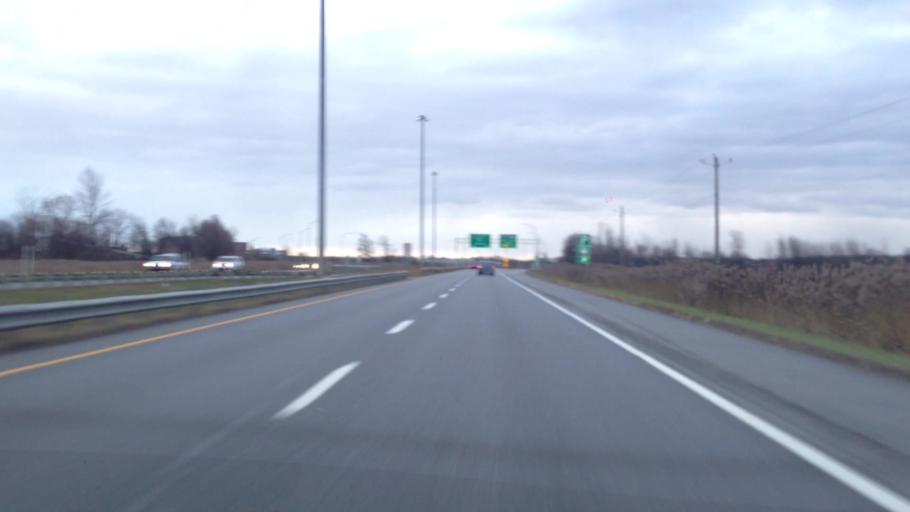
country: CA
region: Quebec
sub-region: Monteregie
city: Vaudreuil-Dorion
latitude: 45.4049
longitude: -74.0683
